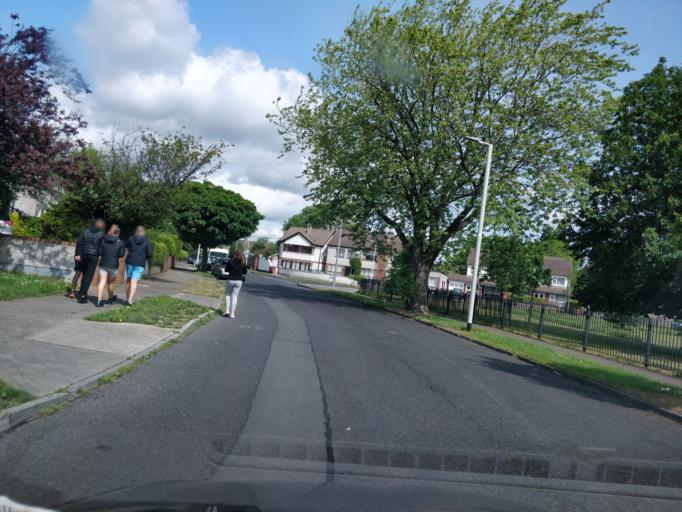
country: IE
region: Leinster
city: Dundrum
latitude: 53.2844
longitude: -6.2584
